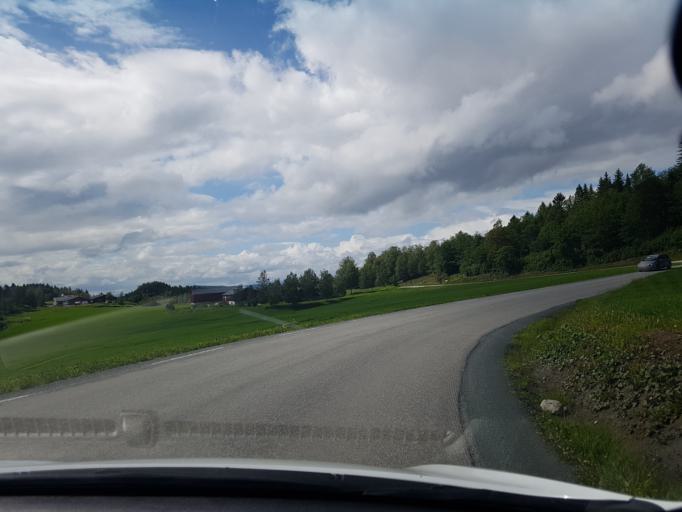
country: NO
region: Nord-Trondelag
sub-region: Stjordal
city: Stjordalshalsen
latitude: 63.5898
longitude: 11.0072
